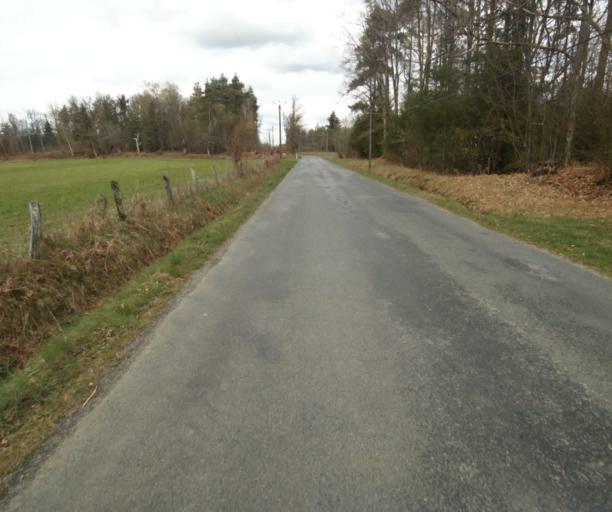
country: FR
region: Limousin
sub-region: Departement de la Correze
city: Argentat
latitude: 45.2158
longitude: 1.9260
